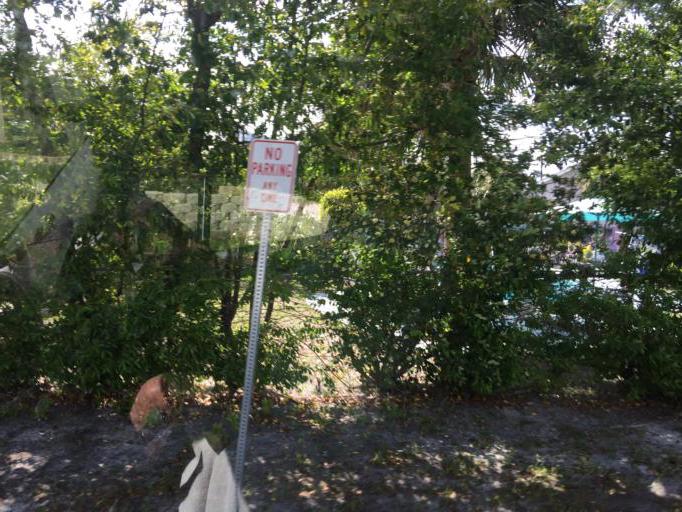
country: US
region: Florida
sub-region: Bay County
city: Laguna Beach
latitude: 30.2203
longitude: -85.8792
